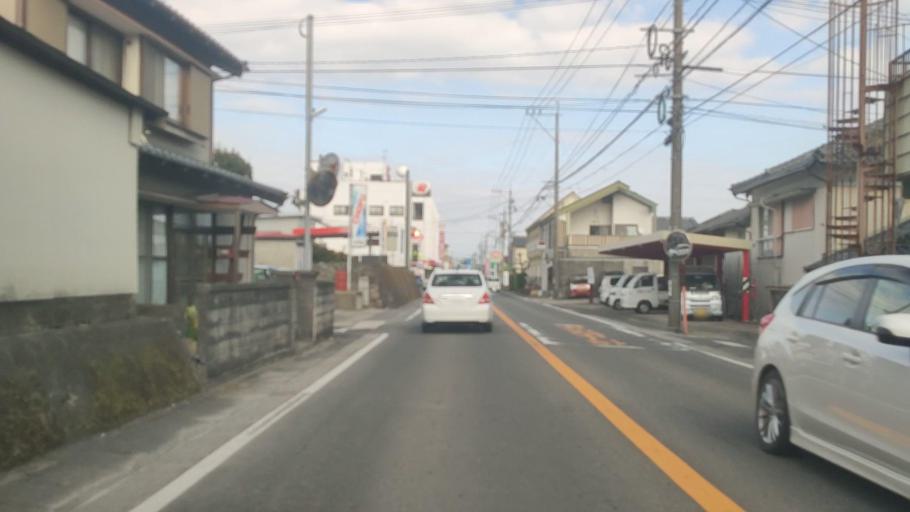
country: JP
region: Nagasaki
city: Shimabara
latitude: 32.7168
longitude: 130.3505
